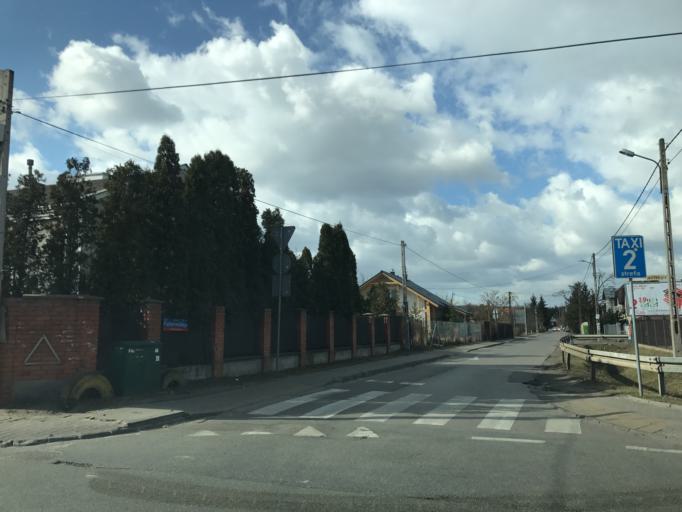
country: PL
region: Masovian Voivodeship
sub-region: Warszawa
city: Rembertow
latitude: 52.2705
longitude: 21.1503
